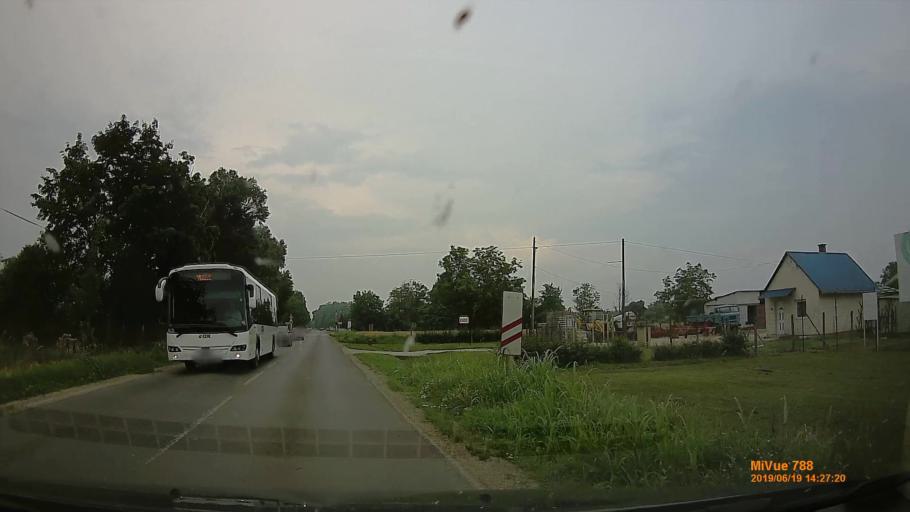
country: HU
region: Baranya
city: Szigetvar
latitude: 46.0420
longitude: 17.7821
